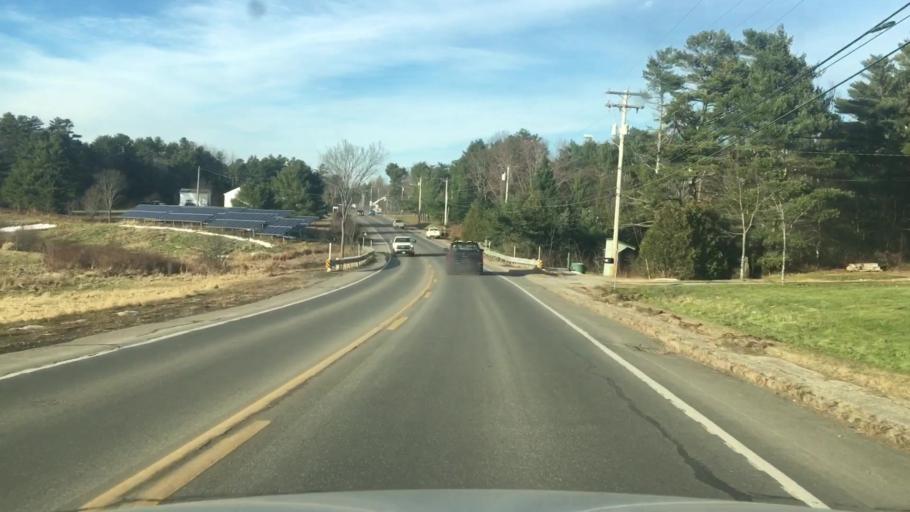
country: US
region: Maine
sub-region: Lincoln County
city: Wiscasset
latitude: 44.0167
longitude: -69.6679
